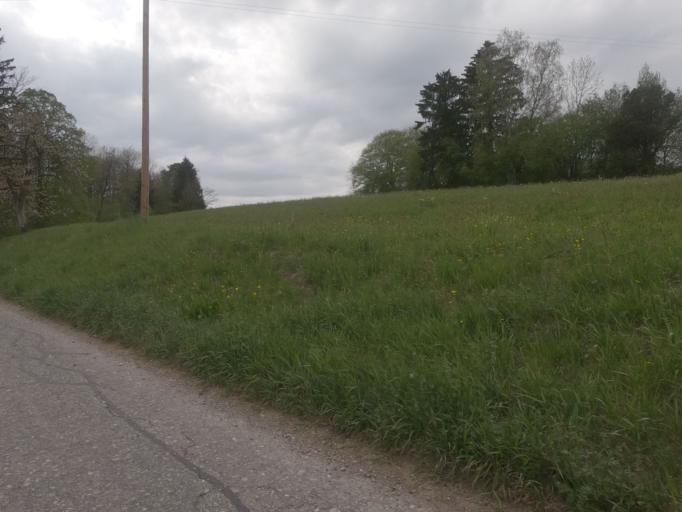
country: CH
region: Solothurn
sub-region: Bezirk Lebern
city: Riedholz
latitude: 47.2411
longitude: 7.5841
